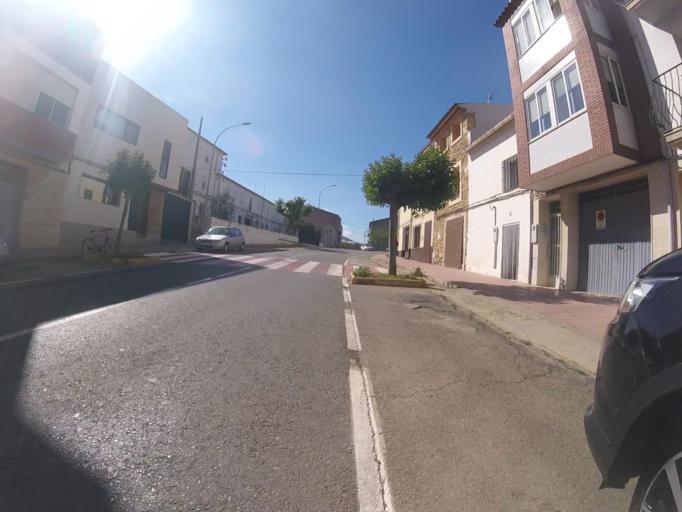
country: ES
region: Valencia
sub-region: Provincia de Castello
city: Albocasser
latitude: 40.3549
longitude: 0.0226
